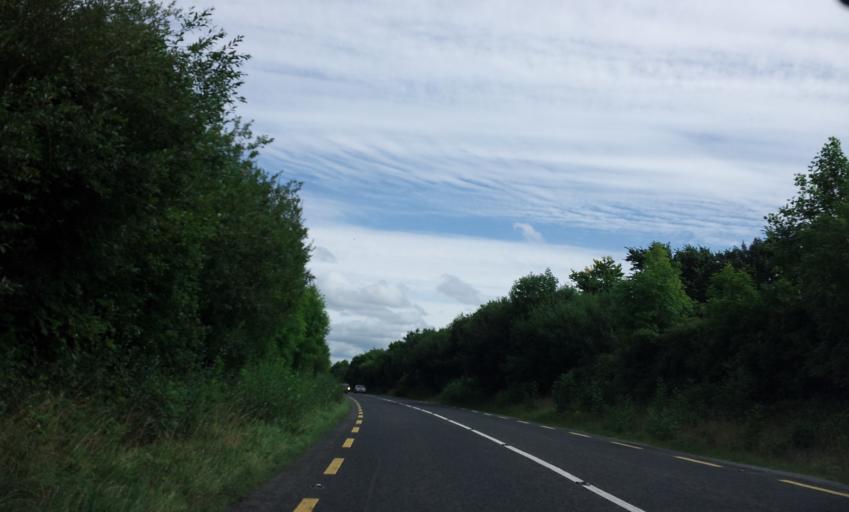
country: IE
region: Munster
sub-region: Ciarrai
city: Cill Airne
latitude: 52.0752
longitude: -9.6473
